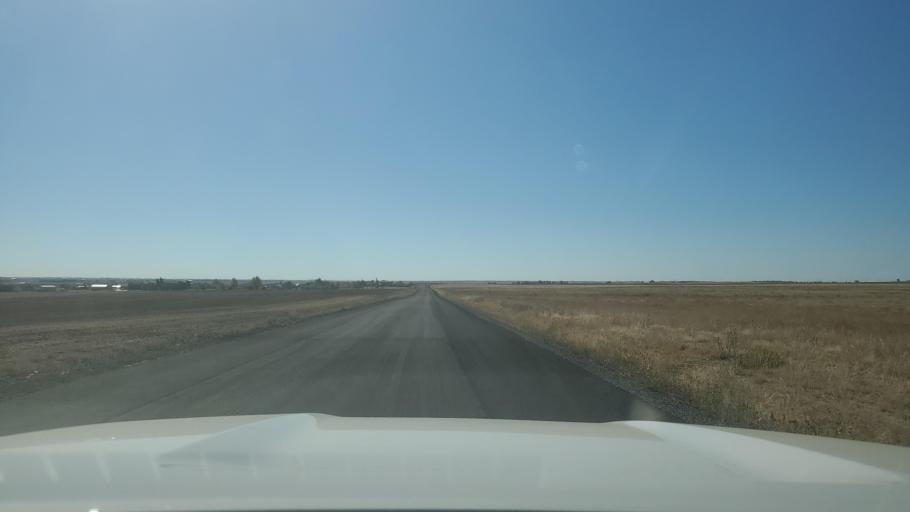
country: US
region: Colorado
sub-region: Adams County
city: Bennett
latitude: 39.7515
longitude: -104.3773
